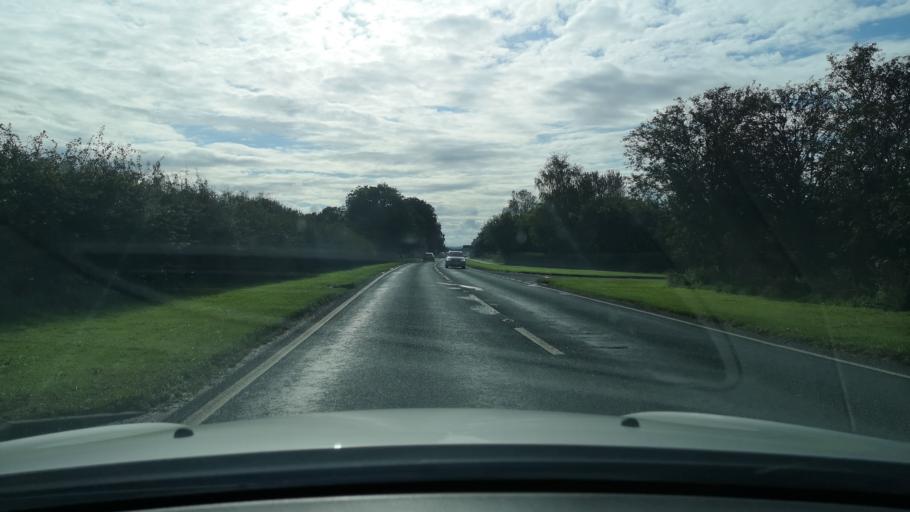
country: GB
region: England
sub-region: East Riding of Yorkshire
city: Leven
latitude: 53.8724
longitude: -0.3389
